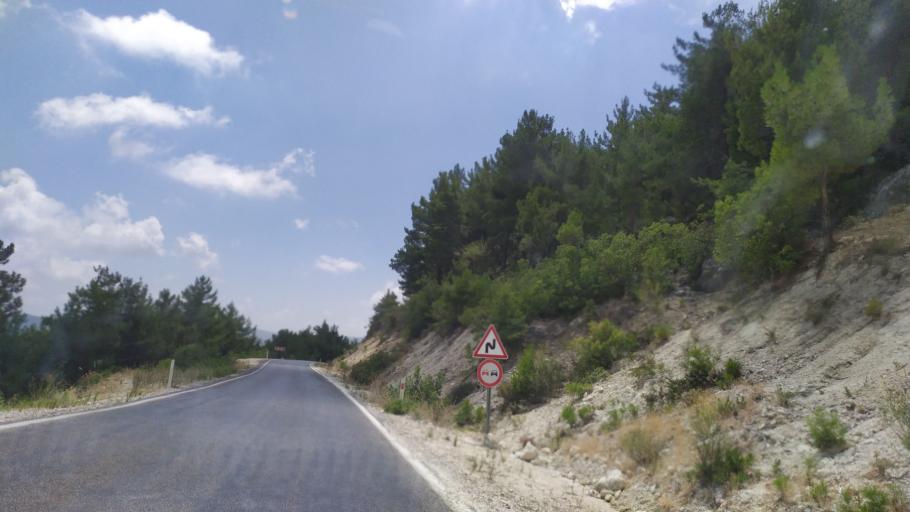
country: TR
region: Mersin
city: Gulnar
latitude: 36.2967
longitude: 33.3796
